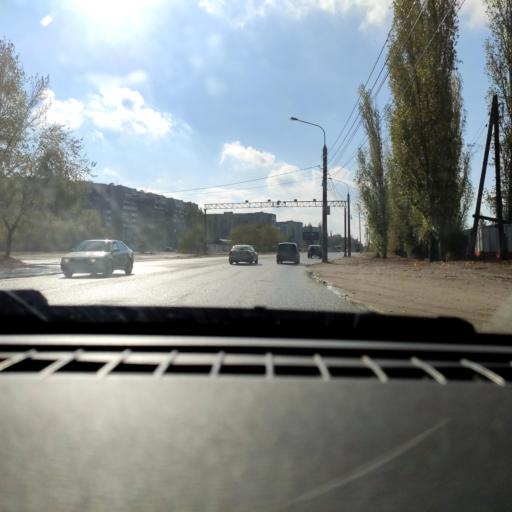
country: RU
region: Voronezj
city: Voronezh
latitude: 51.6446
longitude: 39.2672
